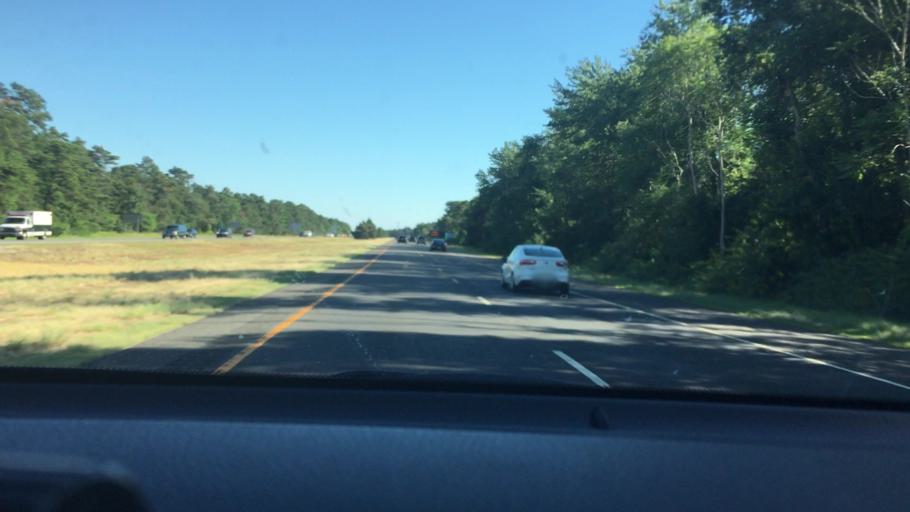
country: US
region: New Jersey
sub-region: Cumberland County
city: Vineland
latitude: 39.4773
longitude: -75.0731
